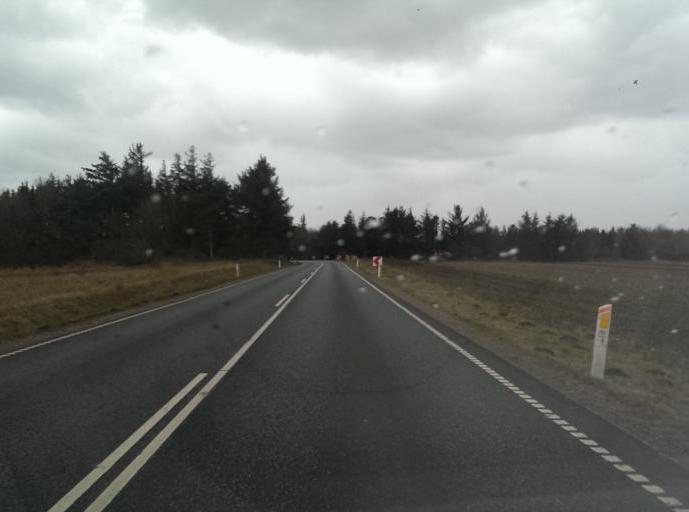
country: DK
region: Central Jutland
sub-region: Holstebro Kommune
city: Ulfborg
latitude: 56.1823
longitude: 8.2901
